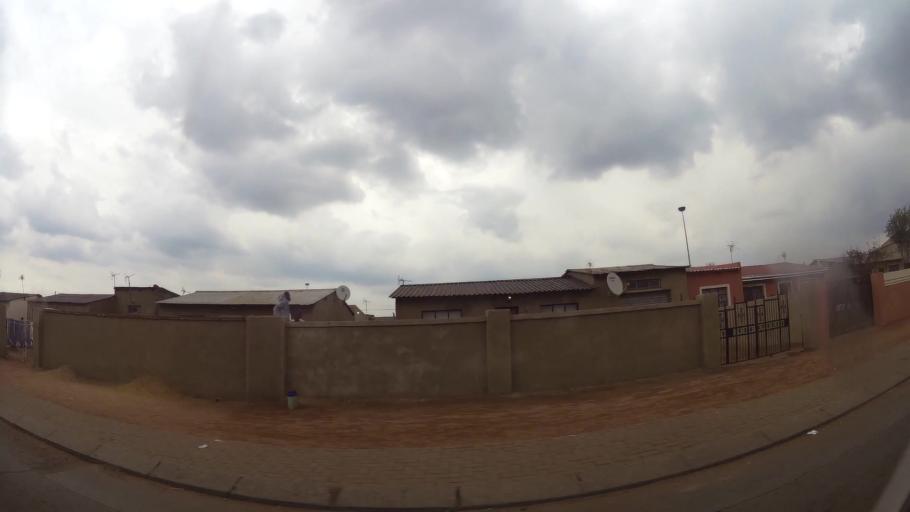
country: ZA
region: Gauteng
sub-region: Ekurhuleni Metropolitan Municipality
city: Germiston
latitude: -26.3577
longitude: 28.1498
